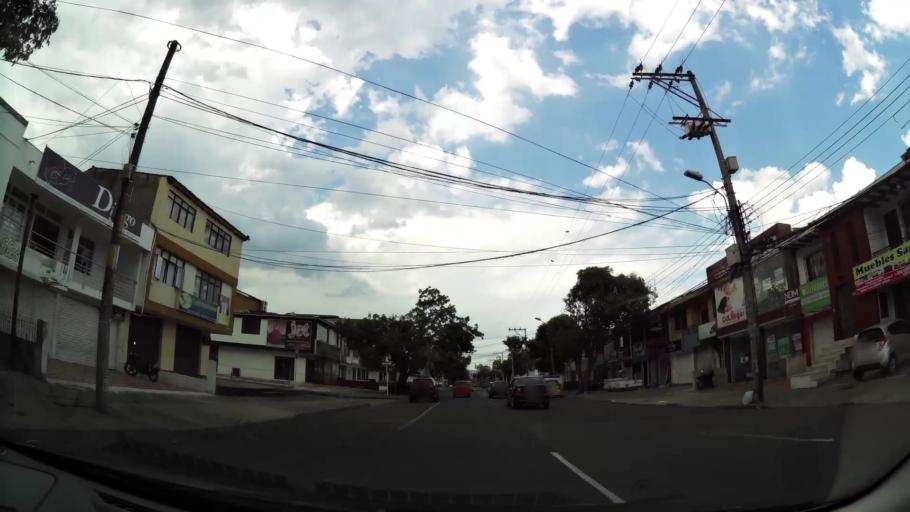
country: CO
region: Valle del Cauca
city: Cali
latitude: 3.4303
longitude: -76.5362
